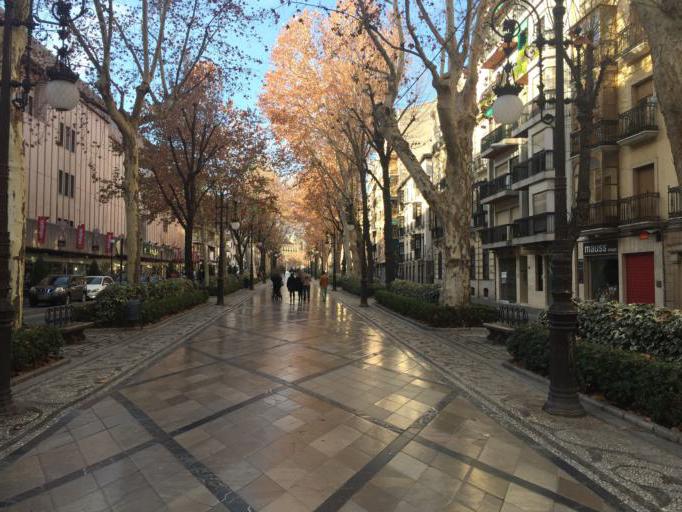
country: ES
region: Andalusia
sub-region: Provincia de Granada
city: Granada
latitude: 37.1704
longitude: -3.5969
